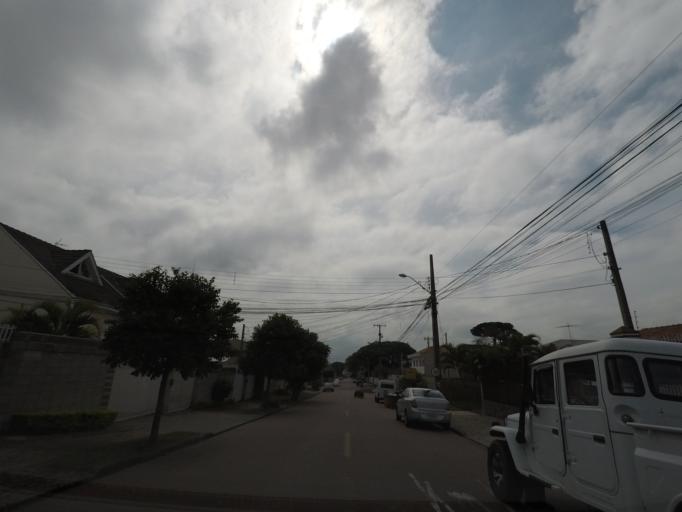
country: BR
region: Parana
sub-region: Curitiba
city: Curitiba
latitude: -25.4916
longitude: -49.3102
